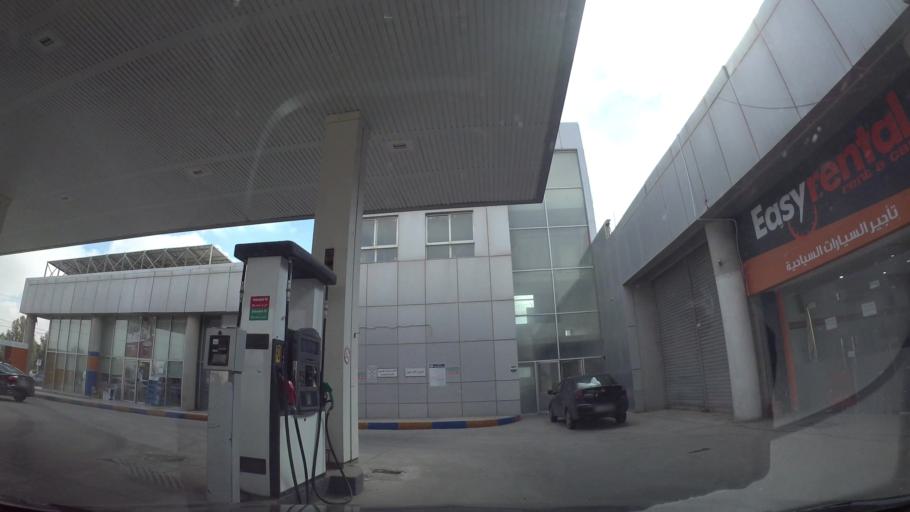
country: JO
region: Amman
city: Al Jizah
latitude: 31.7311
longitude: 35.9437
